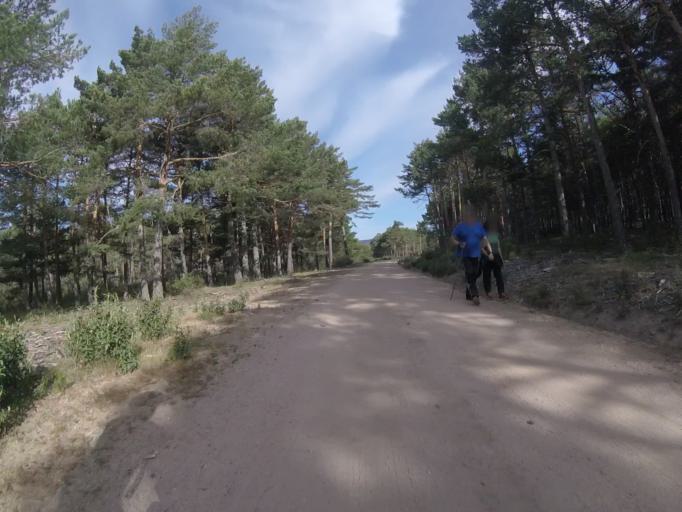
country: ES
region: Castille and Leon
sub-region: Provincia de Avila
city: Peguerinos
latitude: 40.6545
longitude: -4.1837
